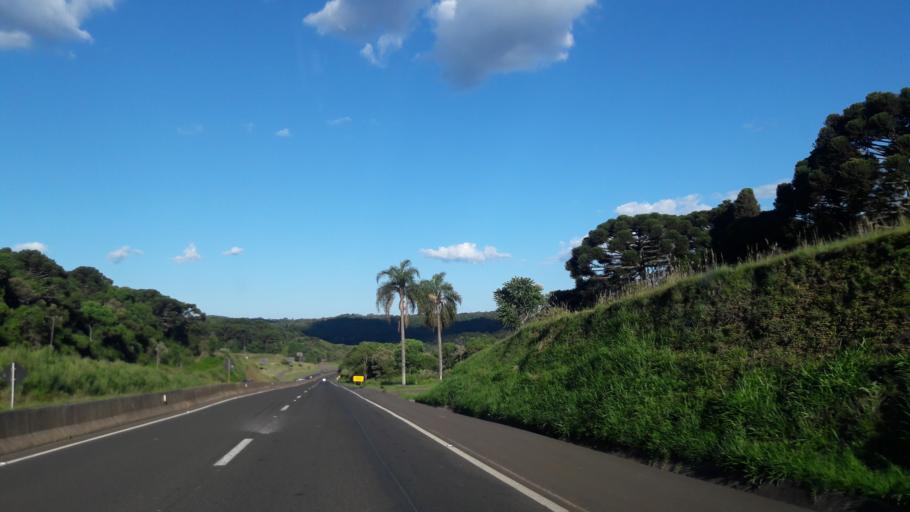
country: BR
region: Parana
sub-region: Guarapuava
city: Guarapuava
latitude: -25.3404
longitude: -51.4218
